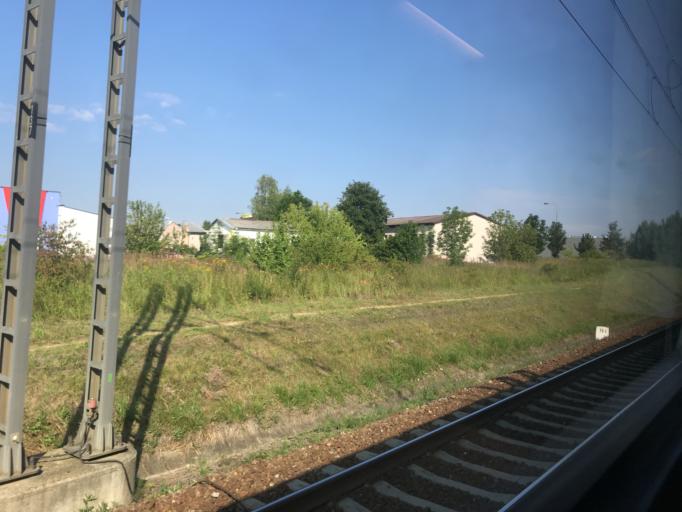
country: CZ
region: Jihocesky
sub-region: Okres Tabor
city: Sezimovo Usti
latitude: 49.3941
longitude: 14.6919
